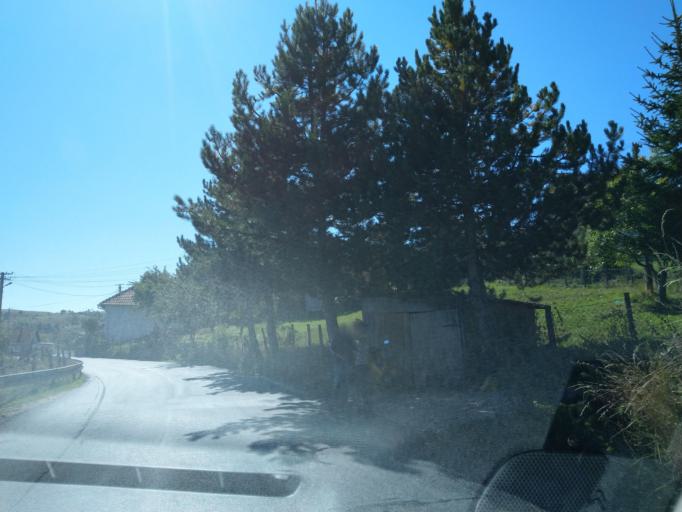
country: RS
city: Sokolovica
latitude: 43.2551
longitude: 20.2297
